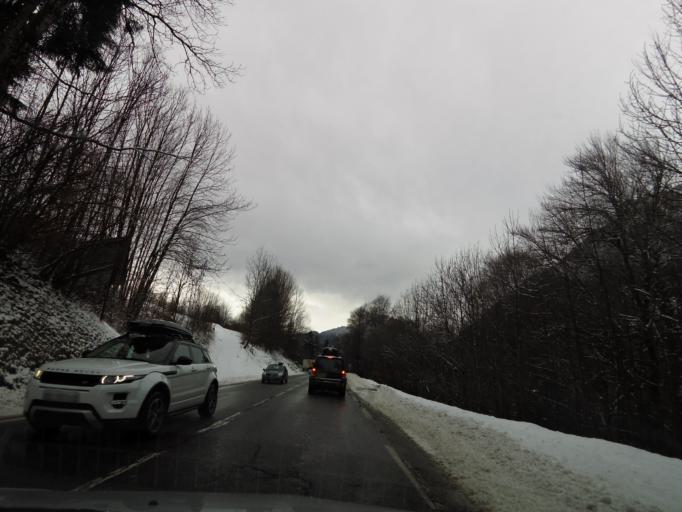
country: FR
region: Rhone-Alpes
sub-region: Departement de la Haute-Savoie
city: Taninges
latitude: 46.1183
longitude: 6.6044
